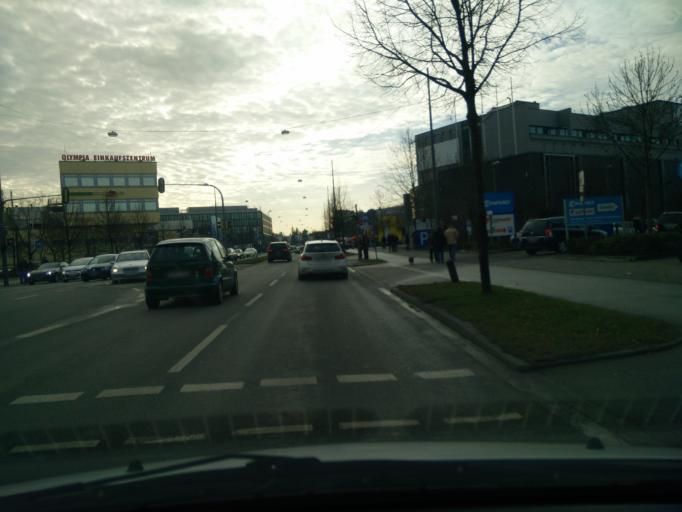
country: DE
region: Bavaria
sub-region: Upper Bavaria
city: Munich
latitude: 48.1851
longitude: 11.5323
